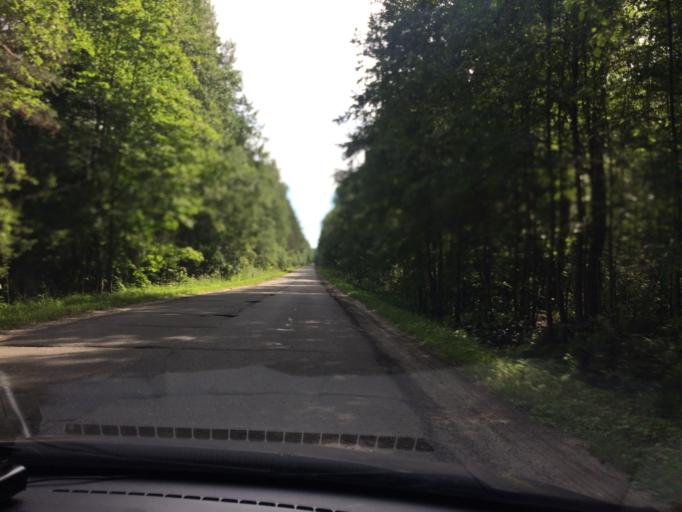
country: RU
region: Mariy-El
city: Surok
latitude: 56.5713
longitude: 48.1884
